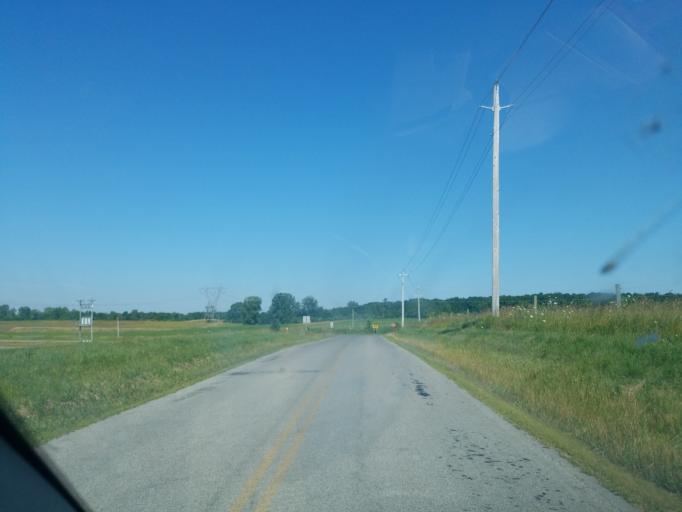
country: US
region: Ohio
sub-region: Logan County
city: Northwood
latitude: 40.4424
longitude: -83.6869
